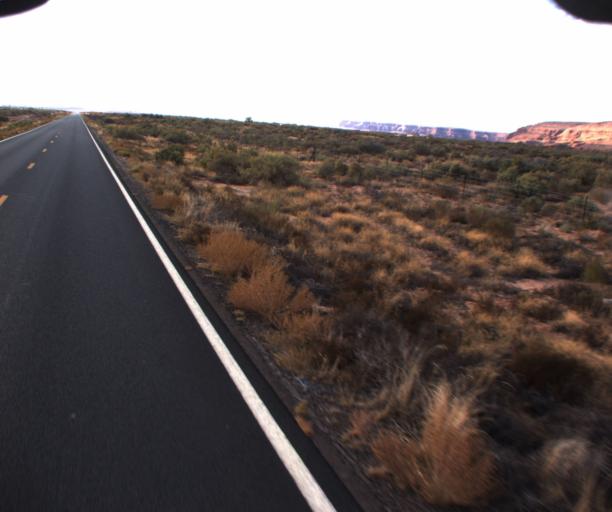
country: US
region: Arizona
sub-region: Apache County
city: Many Farms
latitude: 36.6596
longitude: -109.5953
